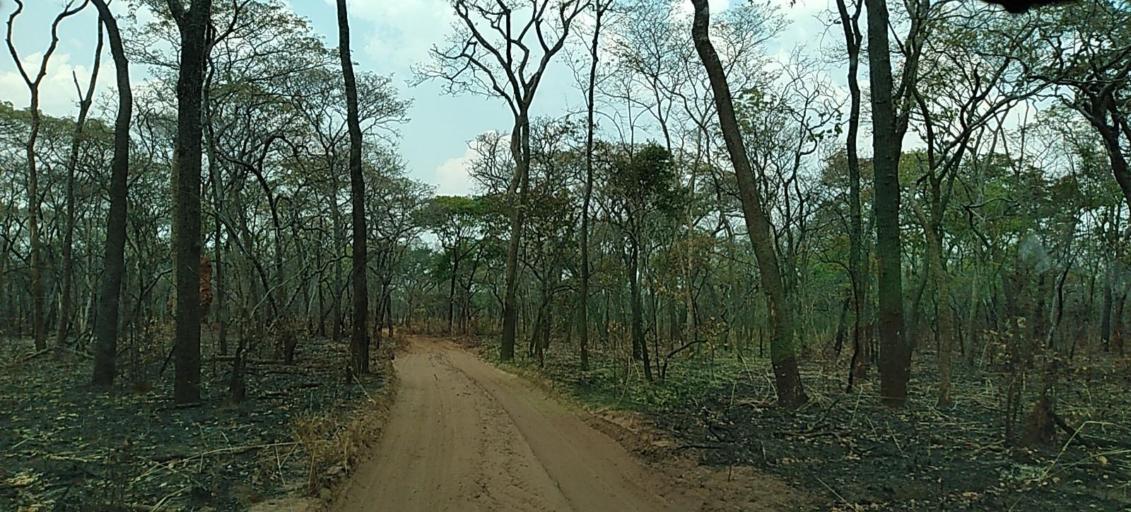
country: ZM
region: North-Western
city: Kabompo
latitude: -13.6101
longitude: 24.3797
